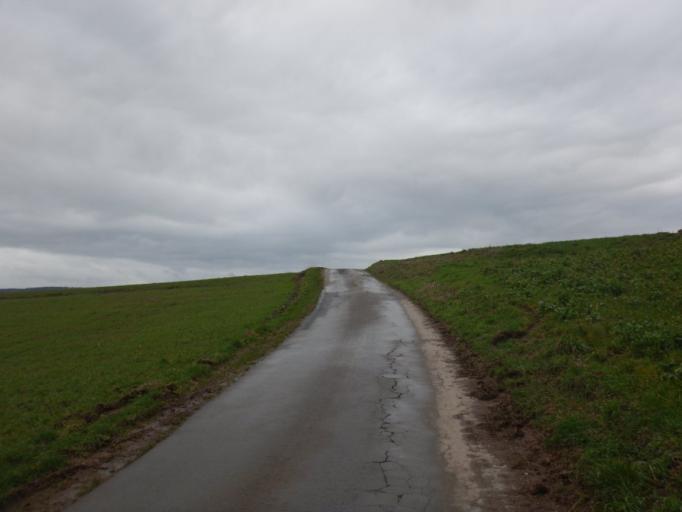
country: BE
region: Wallonia
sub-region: Province du Luxembourg
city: Attert
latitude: 49.7732
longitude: 5.7996
